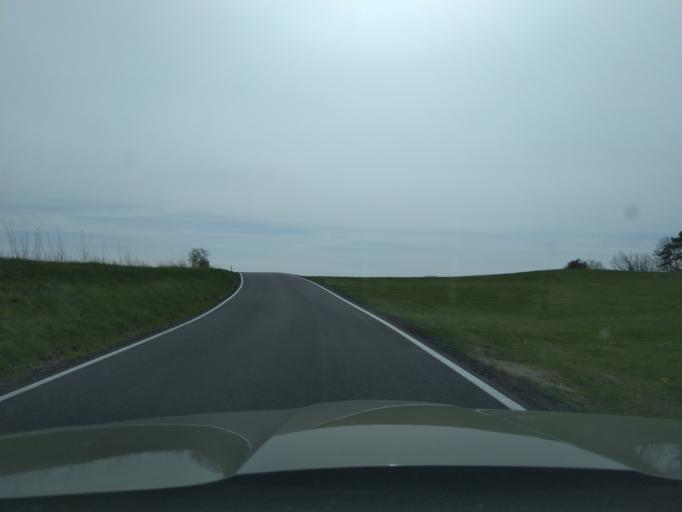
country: CZ
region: Jihocesky
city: Vacov
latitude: 49.1243
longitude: 13.7414
